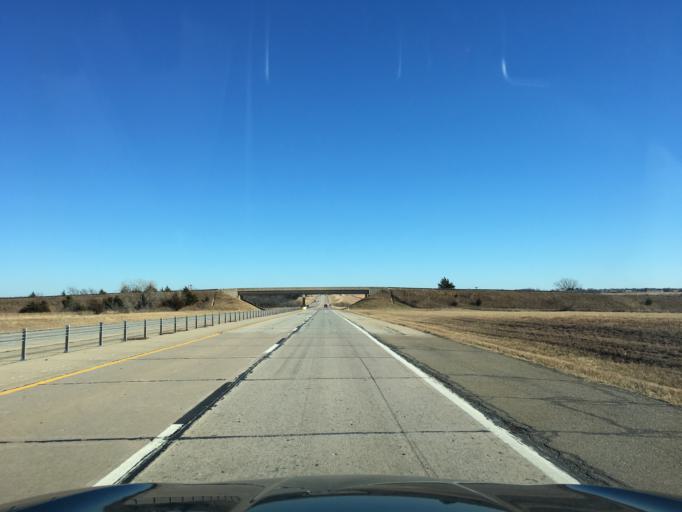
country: US
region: Oklahoma
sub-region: Pawnee County
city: Pawnee
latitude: 36.2252
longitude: -96.8572
